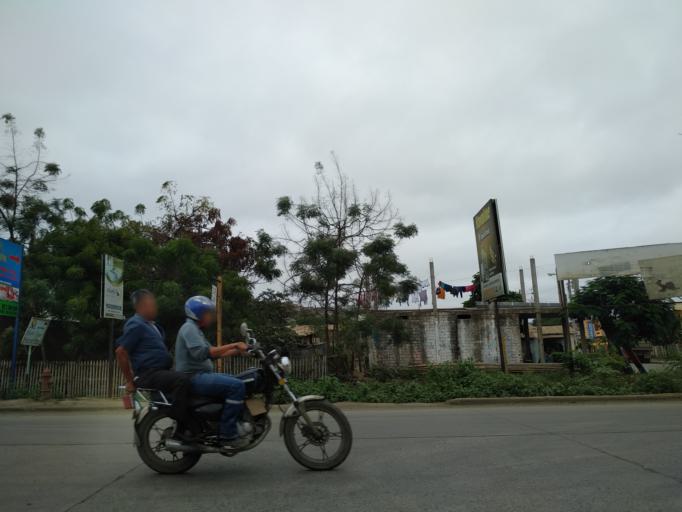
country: EC
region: Manabi
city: Jipijapa
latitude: -1.5534
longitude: -80.8080
